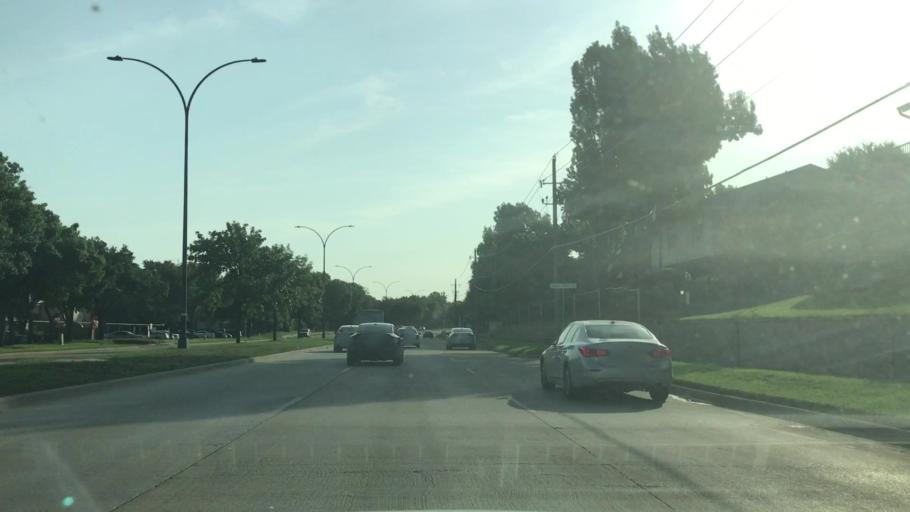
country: US
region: Texas
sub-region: Tarrant County
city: Arlington
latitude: 32.7839
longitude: -97.1130
